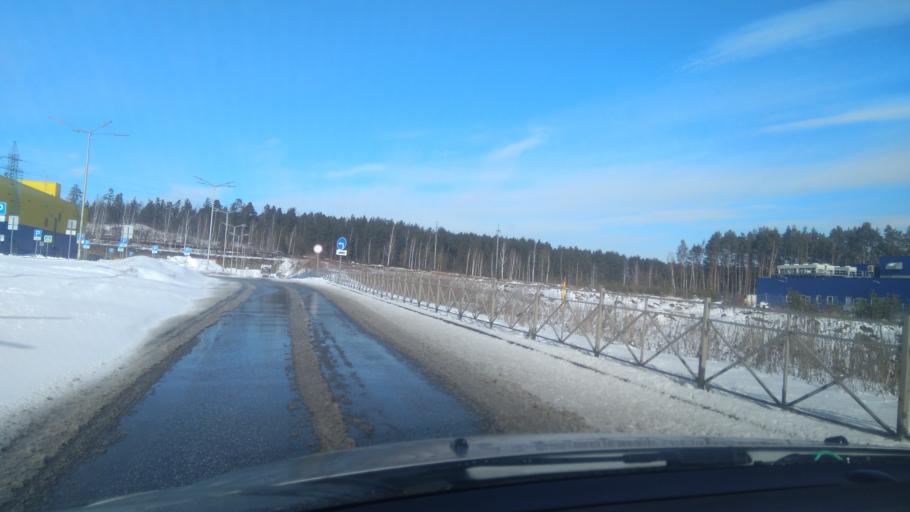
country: RU
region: Sverdlovsk
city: Istok
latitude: 56.8236
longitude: 60.7101
